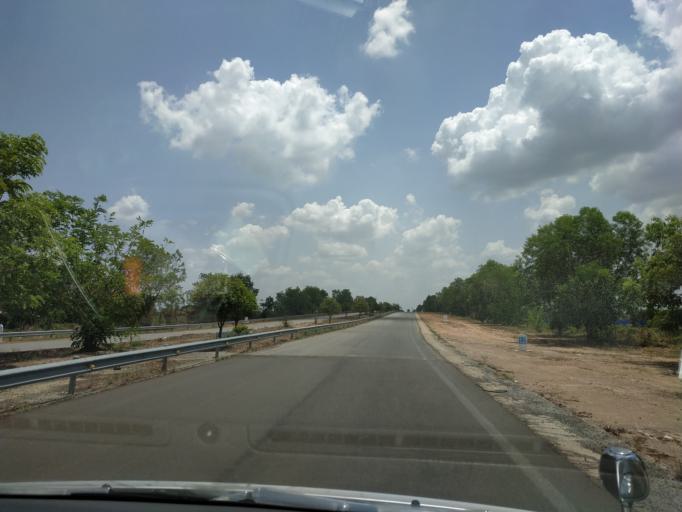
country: MM
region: Bago
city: Thanatpin
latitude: 17.1060
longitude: 96.1807
